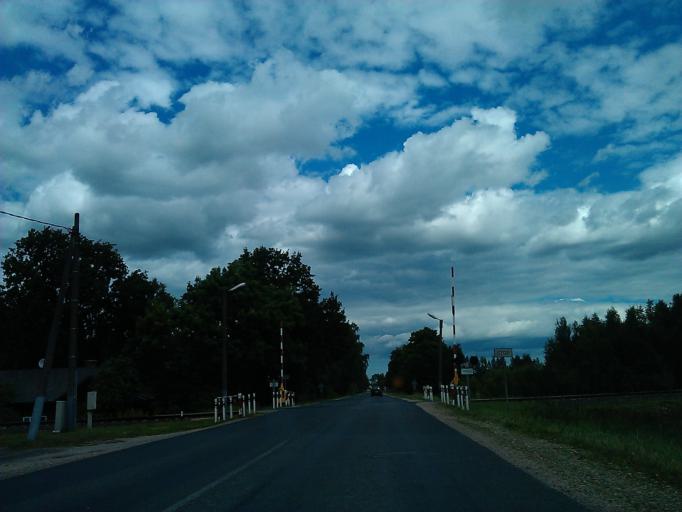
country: LV
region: Jelgava
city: Jelgava
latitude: 56.6460
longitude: 23.6234
